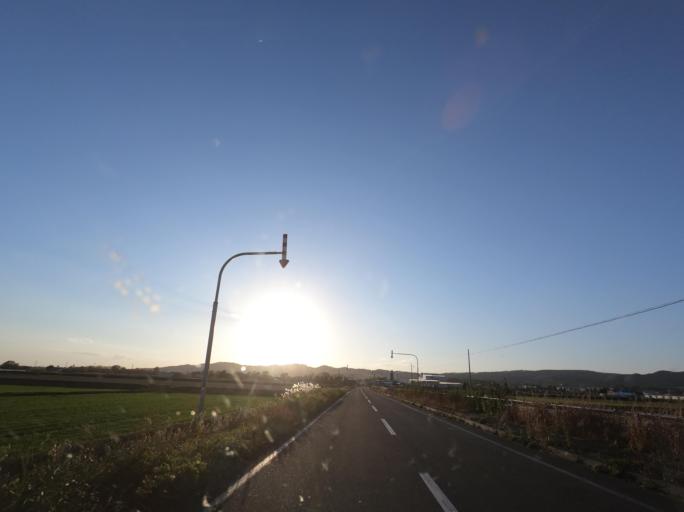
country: JP
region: Hokkaido
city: Chitose
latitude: 42.9751
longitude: 141.8011
